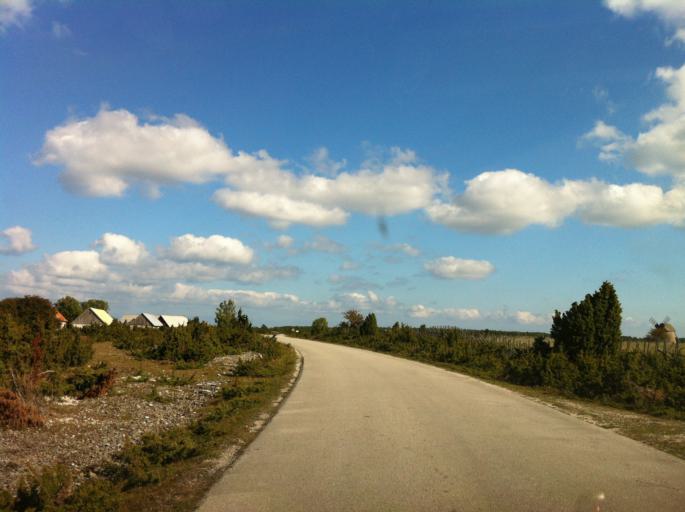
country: SE
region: Gotland
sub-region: Gotland
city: Slite
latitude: 57.9829
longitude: 19.1614
